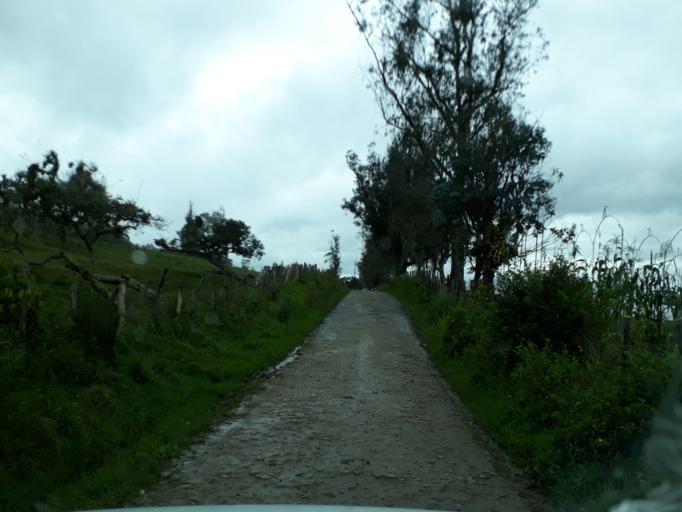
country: CO
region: Cundinamarca
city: Gacheta
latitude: 4.8692
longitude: -73.6329
